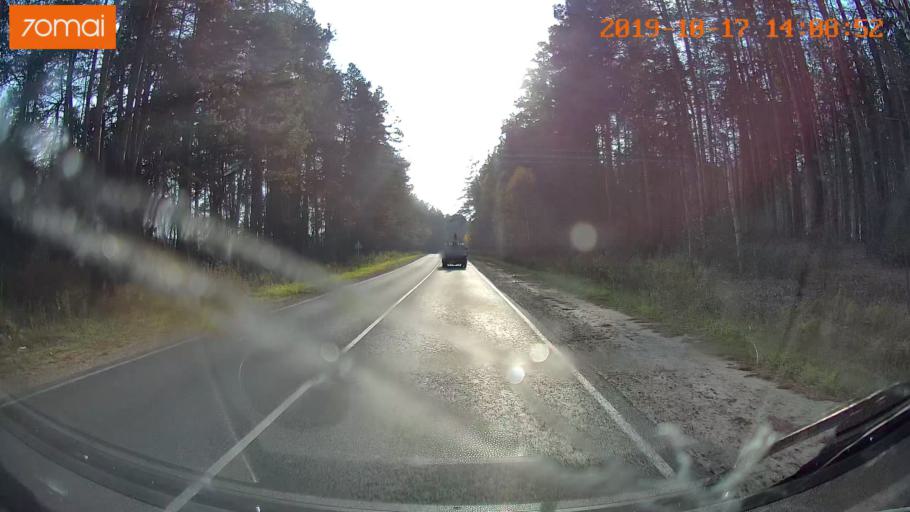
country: RU
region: Rjazan
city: Spas-Klepiki
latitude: 55.0952
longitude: 40.0645
